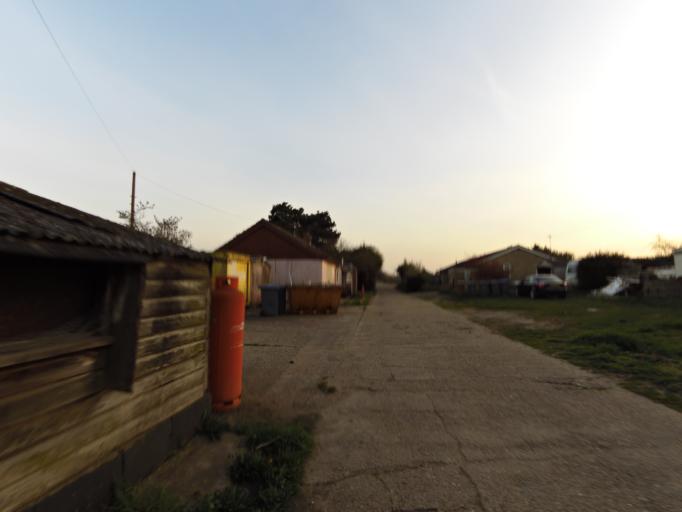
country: GB
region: England
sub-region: Suffolk
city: Kesgrave
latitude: 52.0270
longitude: 1.2295
